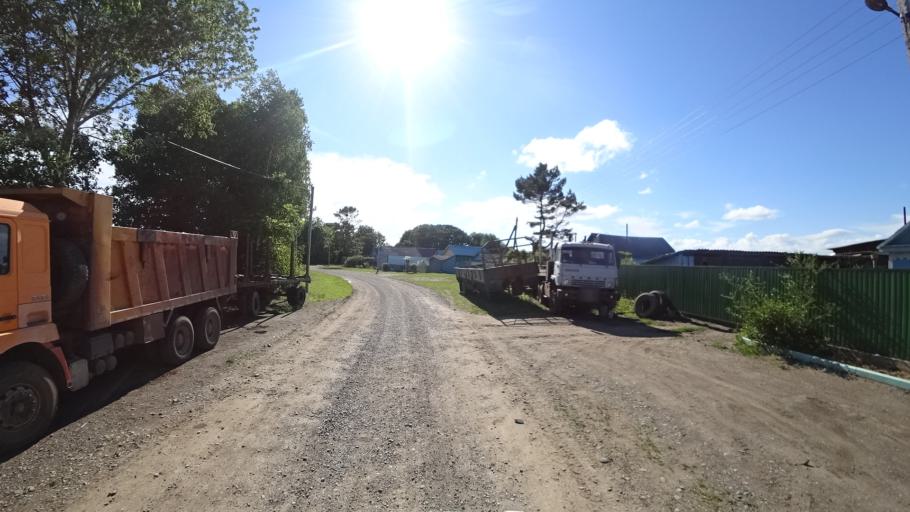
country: RU
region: Khabarovsk Krai
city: Khor
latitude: 47.8865
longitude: 135.0027
